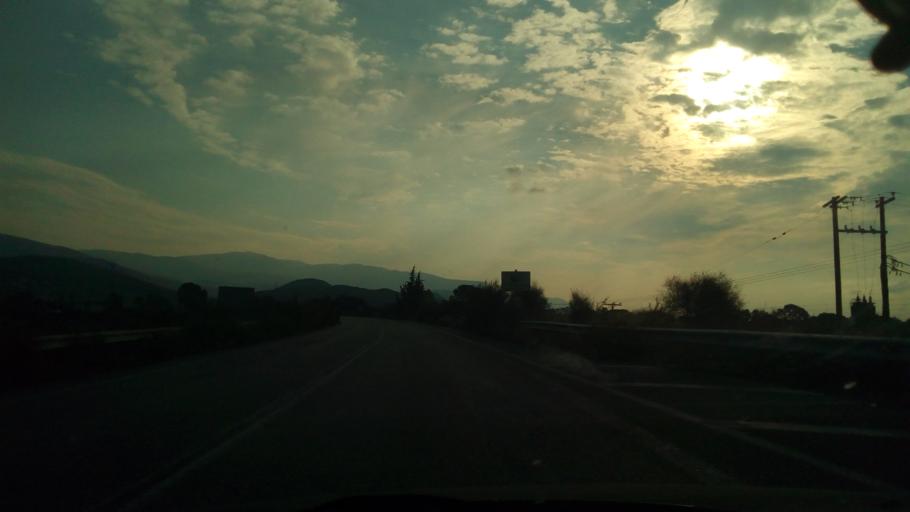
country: GR
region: West Greece
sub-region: Nomos Aitolias kai Akarnanias
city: Nafpaktos
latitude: 38.4062
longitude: 21.8717
